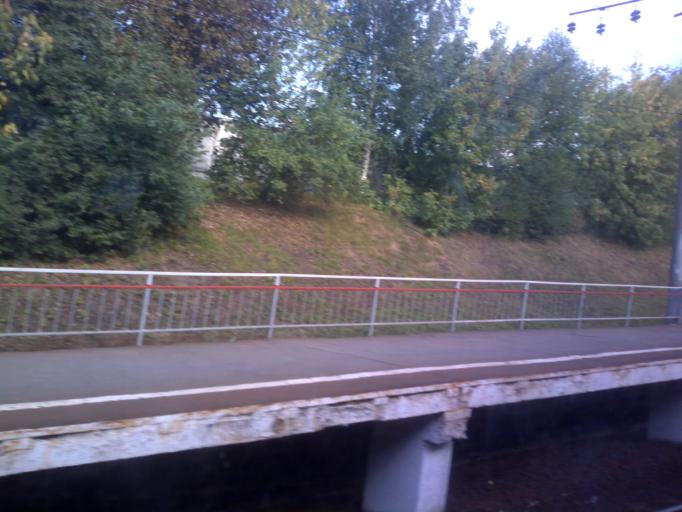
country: RU
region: Moscow
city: Nagornyy
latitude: 55.6307
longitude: 37.6276
